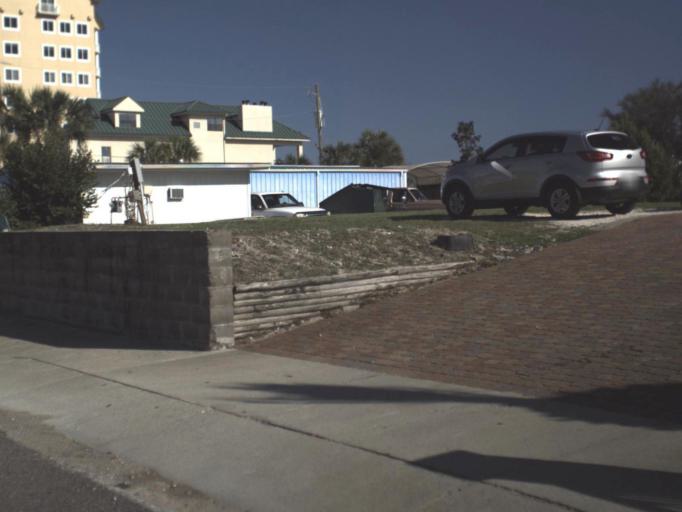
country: US
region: Florida
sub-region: Okaloosa County
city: Destin
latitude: 30.3914
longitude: -86.4927
